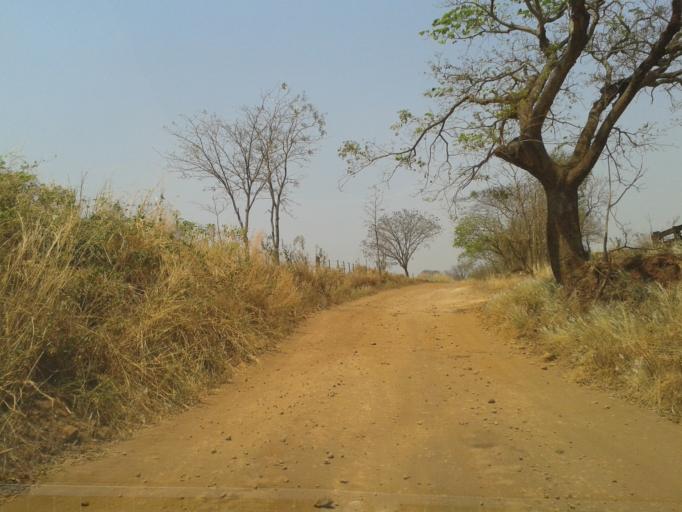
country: BR
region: Minas Gerais
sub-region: Centralina
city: Centralina
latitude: -18.7065
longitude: -49.2353
